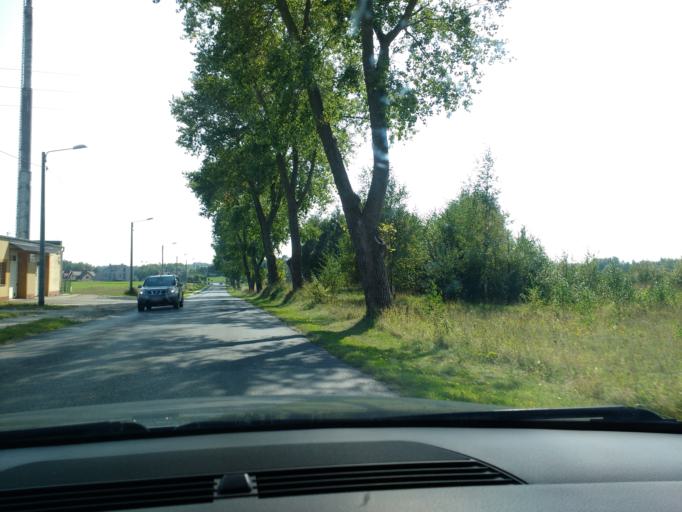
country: PL
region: Pomeranian Voivodeship
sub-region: Powiat wejherowski
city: Bojano
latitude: 54.4969
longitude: 18.4175
